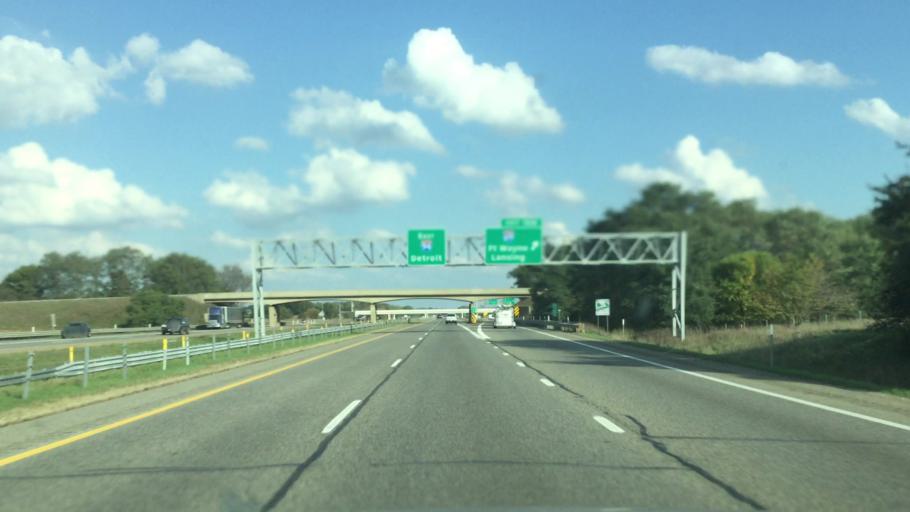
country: US
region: Michigan
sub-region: Calhoun County
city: Marshall
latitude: 42.2973
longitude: -85.0062
